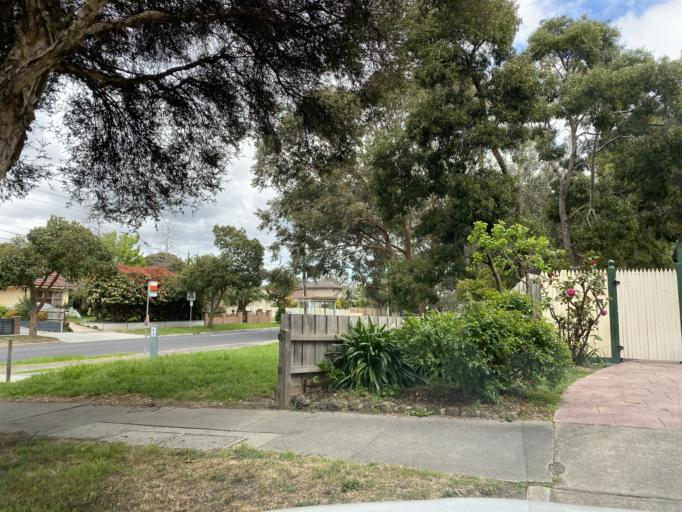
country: AU
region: Victoria
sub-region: Whitehorse
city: Burwood
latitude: -37.8448
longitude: 145.1261
